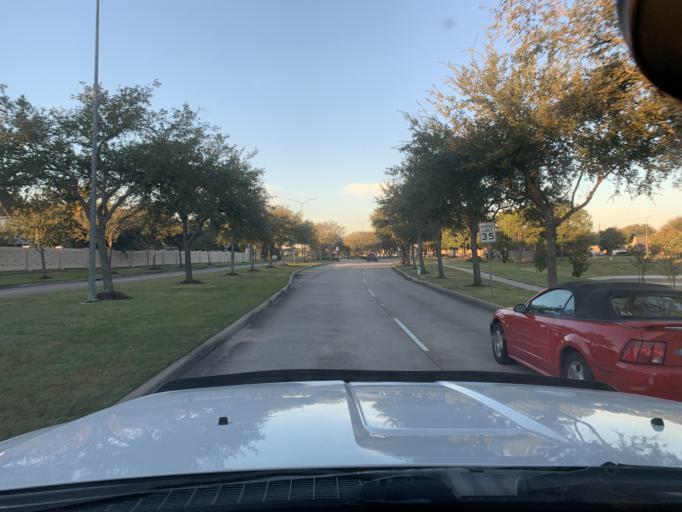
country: US
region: Texas
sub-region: Fort Bend County
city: Four Corners
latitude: 29.6498
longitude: -95.6364
